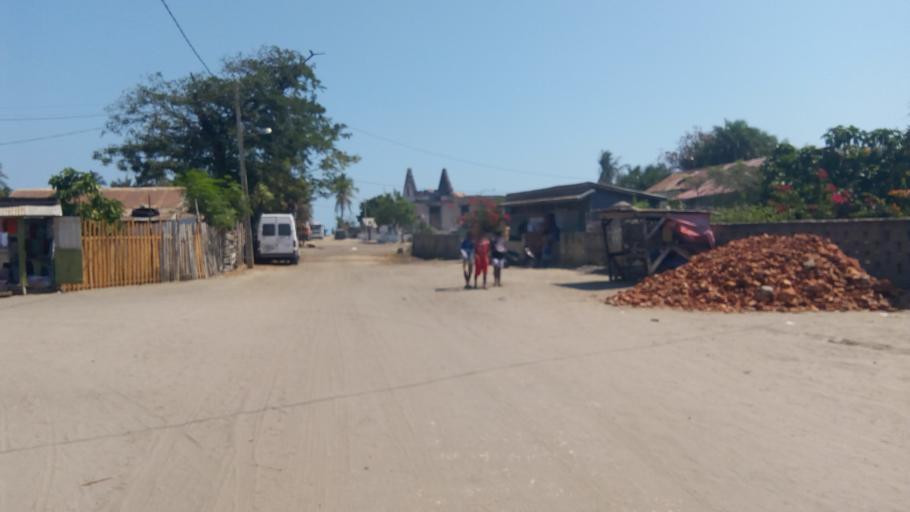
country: MG
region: Menabe
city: Morondava
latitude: -20.2899
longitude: 44.2773
